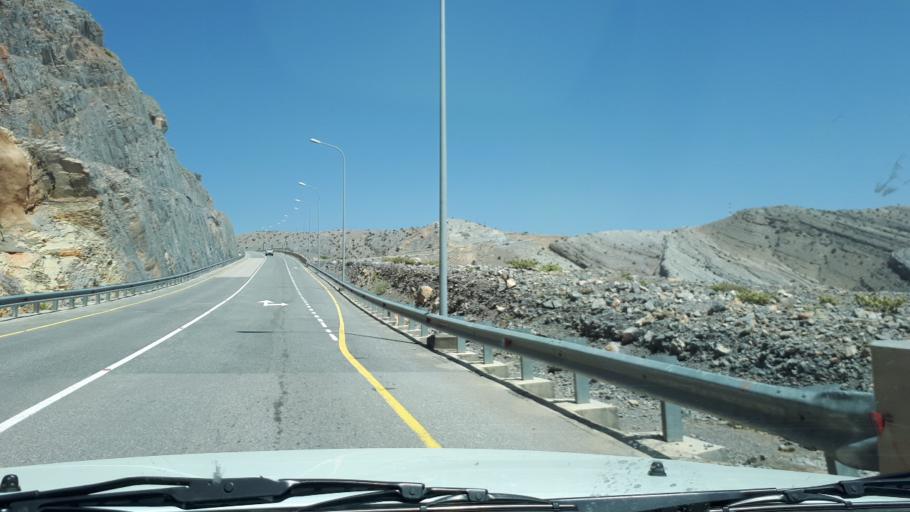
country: OM
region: Muhafazat ad Dakhiliyah
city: Izki
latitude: 23.0121
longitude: 57.6985
